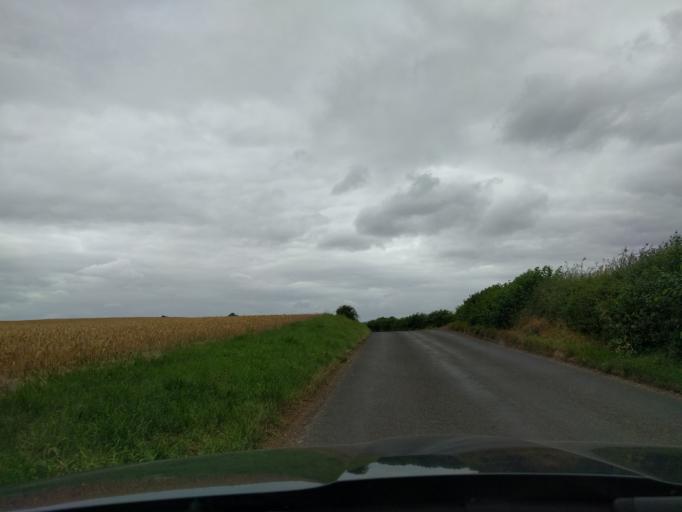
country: GB
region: England
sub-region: Northumberland
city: Berwick-Upon-Tweed
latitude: 55.7496
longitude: -2.0827
